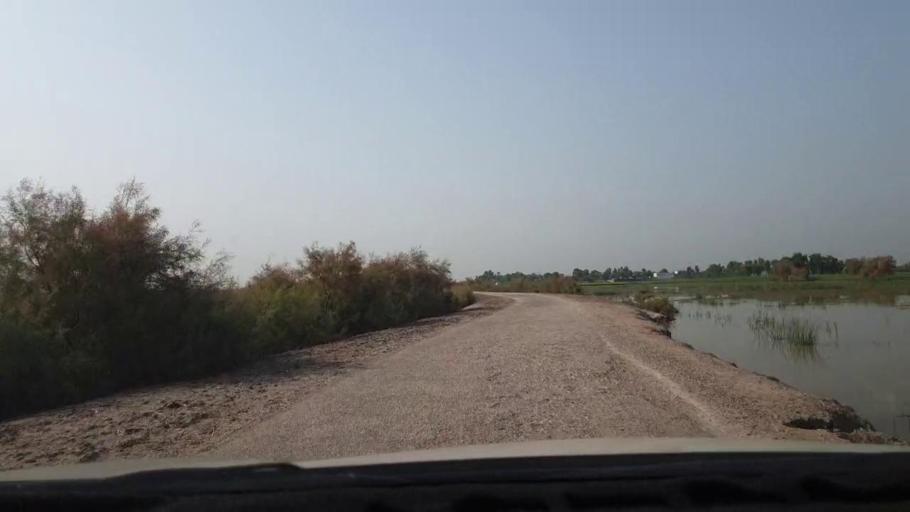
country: PK
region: Sindh
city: Goth Garelo
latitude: 27.4929
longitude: 68.1138
